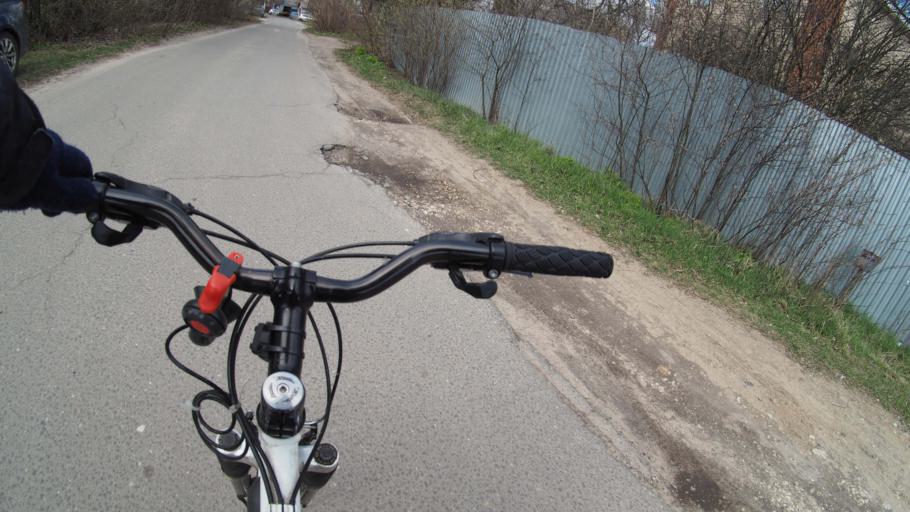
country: RU
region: Moskovskaya
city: Ramenskoye
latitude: 55.5533
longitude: 38.2817
